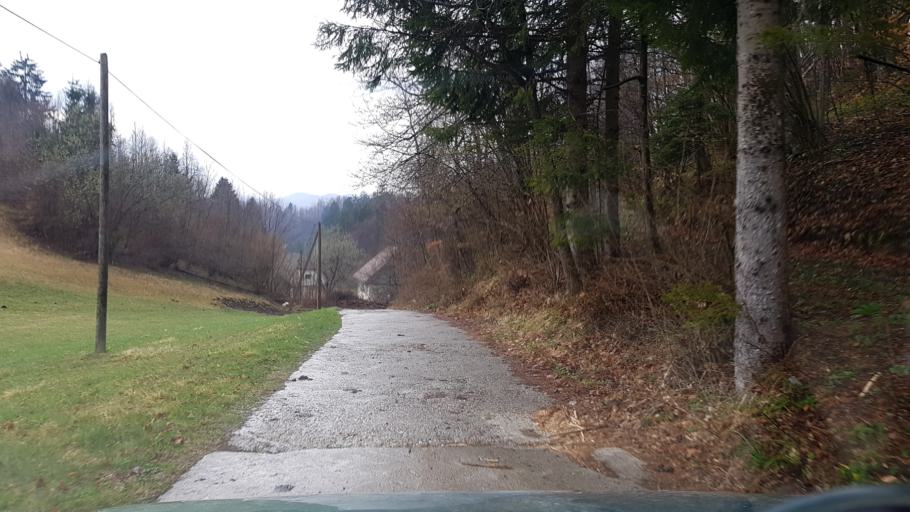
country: SI
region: Cerkno
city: Cerkno
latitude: 46.1359
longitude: 13.8559
